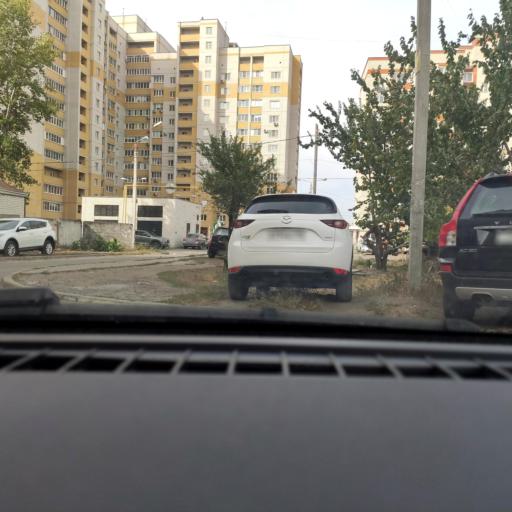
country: RU
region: Voronezj
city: Voronezh
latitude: 51.6782
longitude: 39.2507
